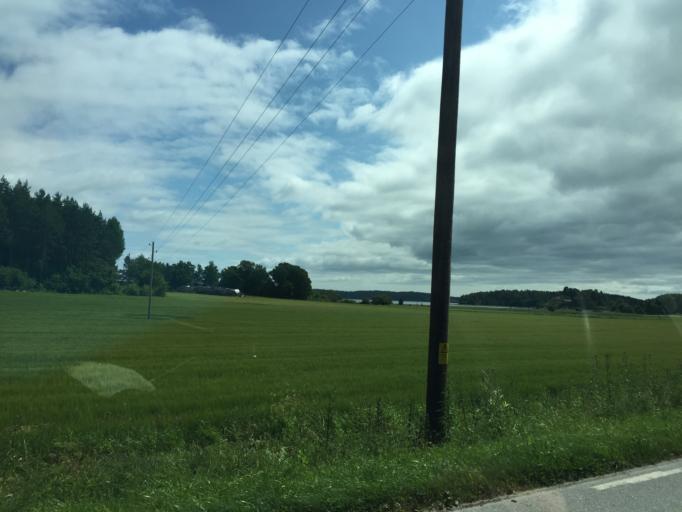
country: SE
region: Soedermanland
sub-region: Trosa Kommun
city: Trosa
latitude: 58.9711
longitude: 17.6938
